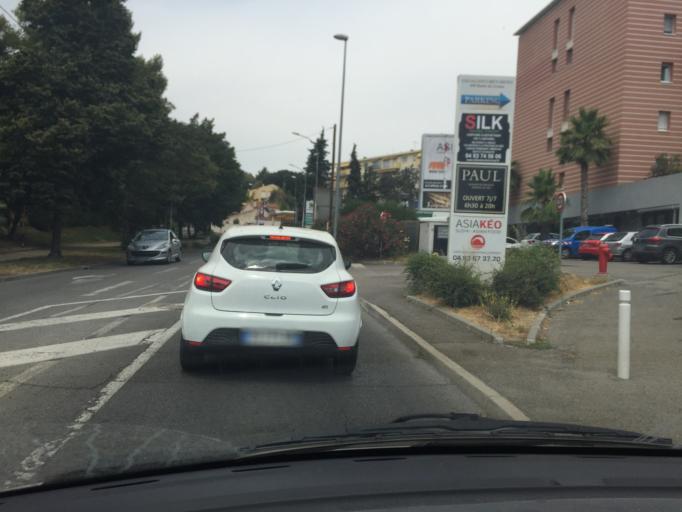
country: FR
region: Provence-Alpes-Cote d'Azur
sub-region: Departement des Alpes-Maritimes
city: Biot
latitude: 43.5937
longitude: 7.0992
